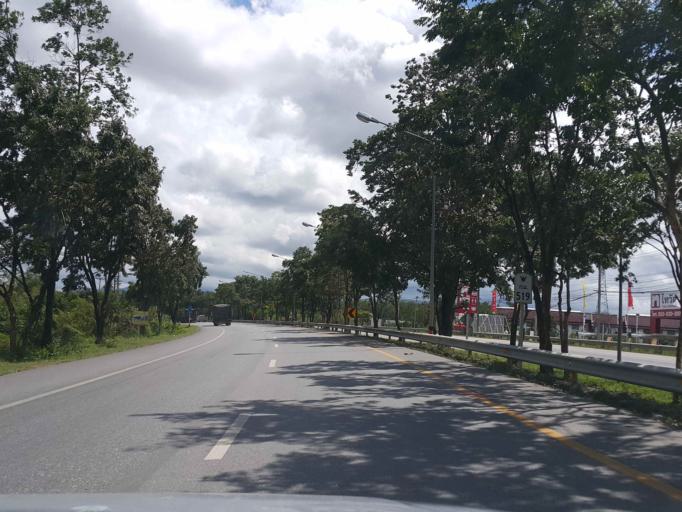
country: TH
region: Tak
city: Tak
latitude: 16.8499
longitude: 99.1126
